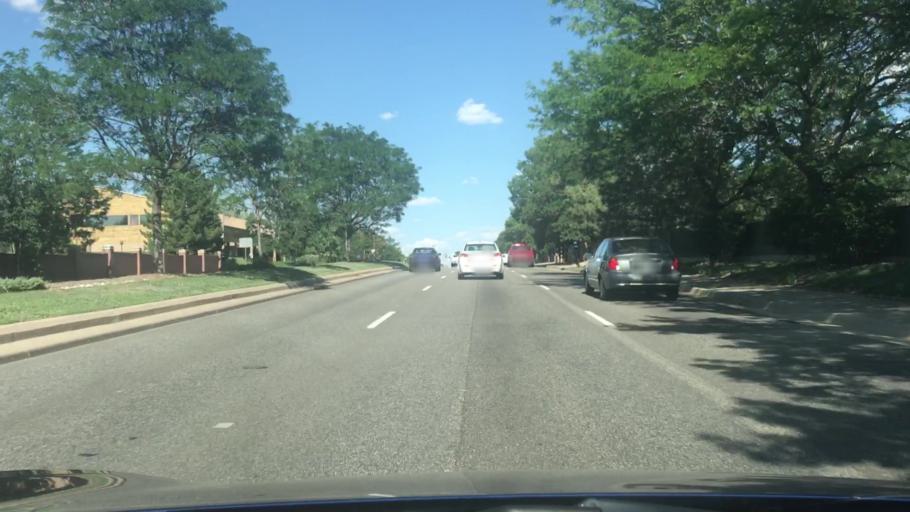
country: US
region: Colorado
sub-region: Arapahoe County
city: Dove Valley
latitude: 39.6530
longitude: -104.8231
